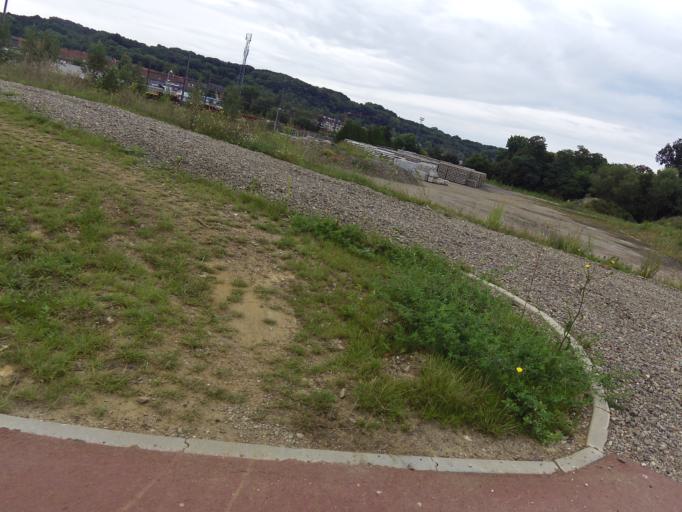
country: BE
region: Flanders
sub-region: Provincie Vlaams-Brabant
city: Aarschot
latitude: 50.9826
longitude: 4.8205
